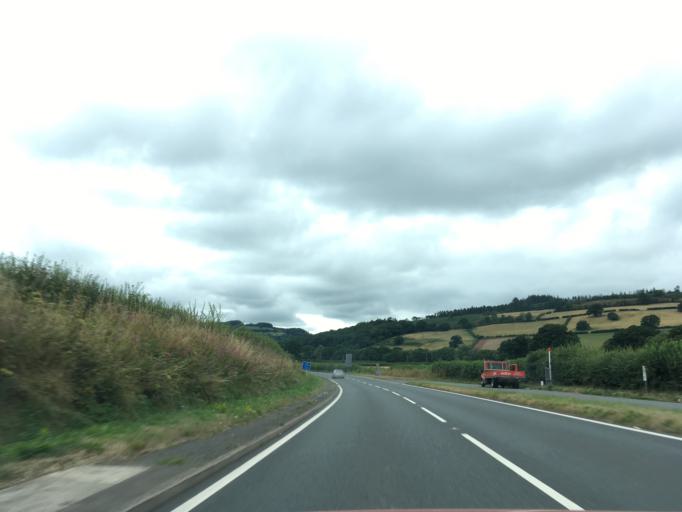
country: GB
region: Wales
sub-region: Sir Powys
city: Brecon
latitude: 51.9479
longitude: -3.4181
